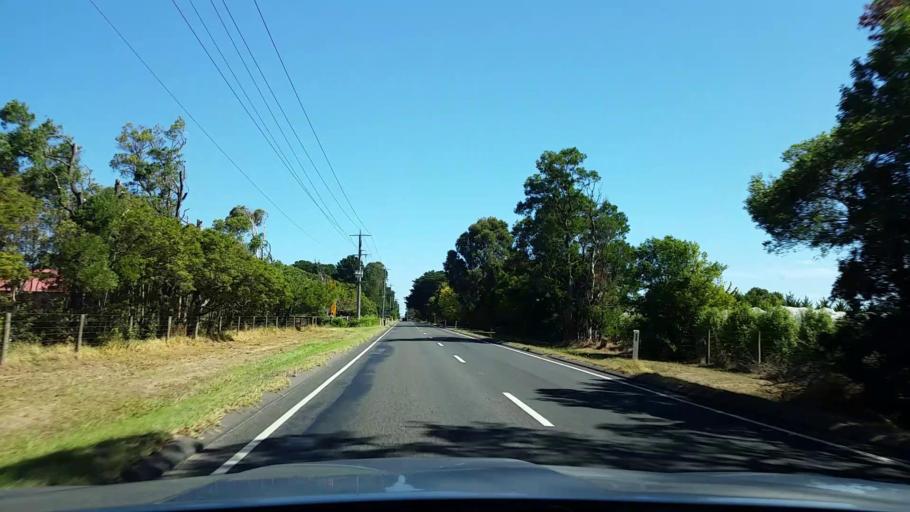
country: AU
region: Victoria
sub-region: Mornington Peninsula
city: Hastings
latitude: -38.2847
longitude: 145.1522
